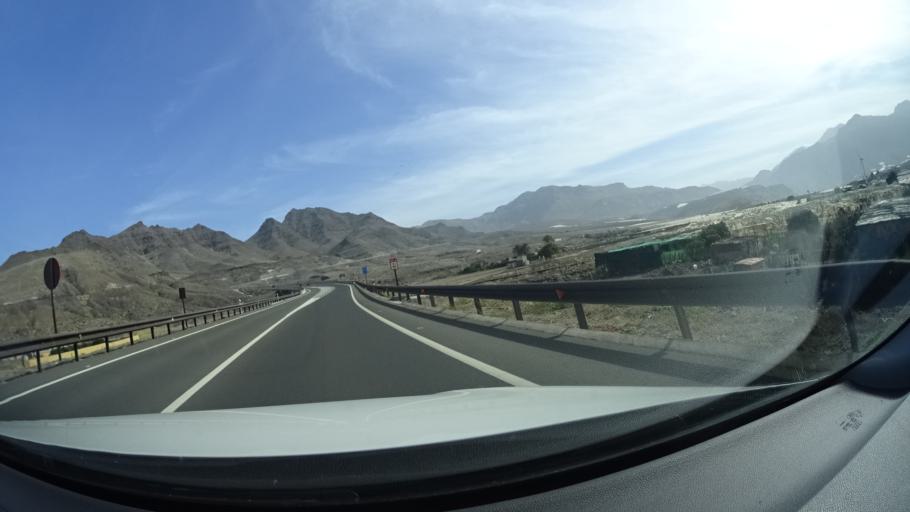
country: ES
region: Canary Islands
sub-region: Provincia de Las Palmas
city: San Nicolas
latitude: 28.0006
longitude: -15.8108
